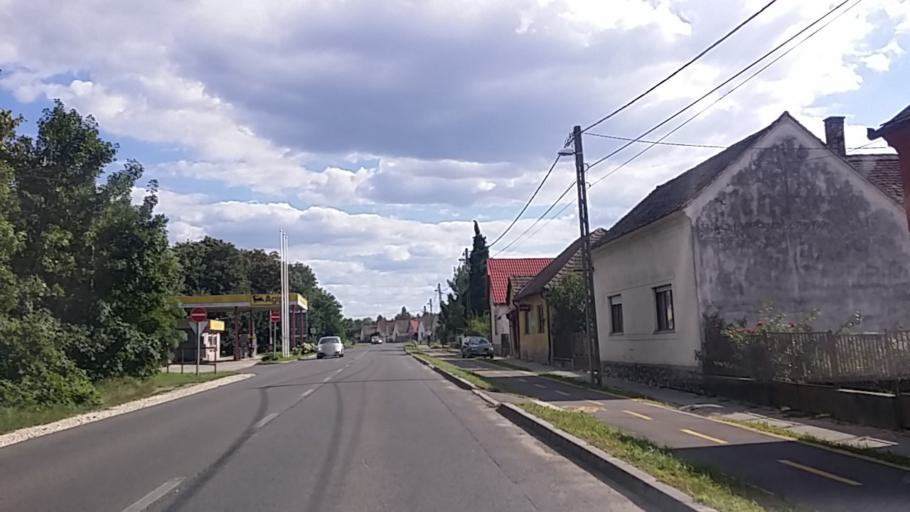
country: HU
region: Tolna
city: Dombovar
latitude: 46.3354
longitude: 18.1270
